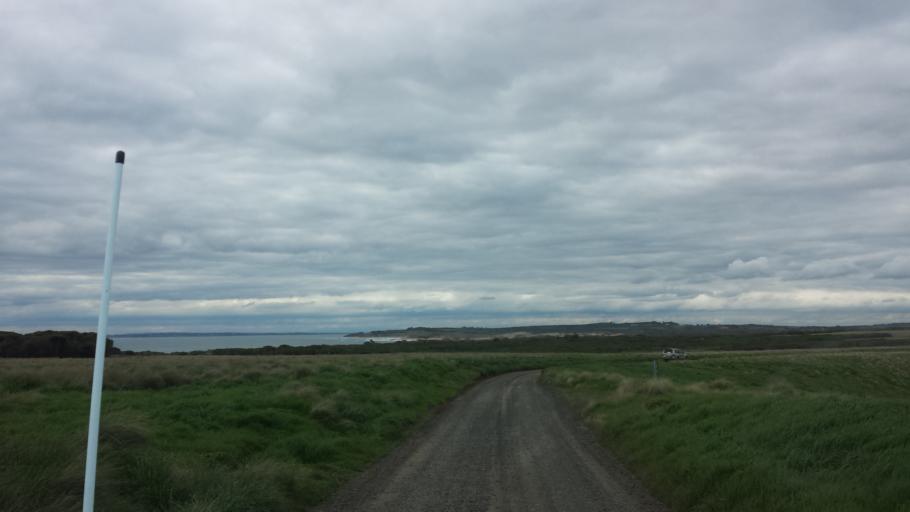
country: AU
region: Victoria
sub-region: Bass Coast
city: Phillip Island
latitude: -38.5163
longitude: 145.1313
